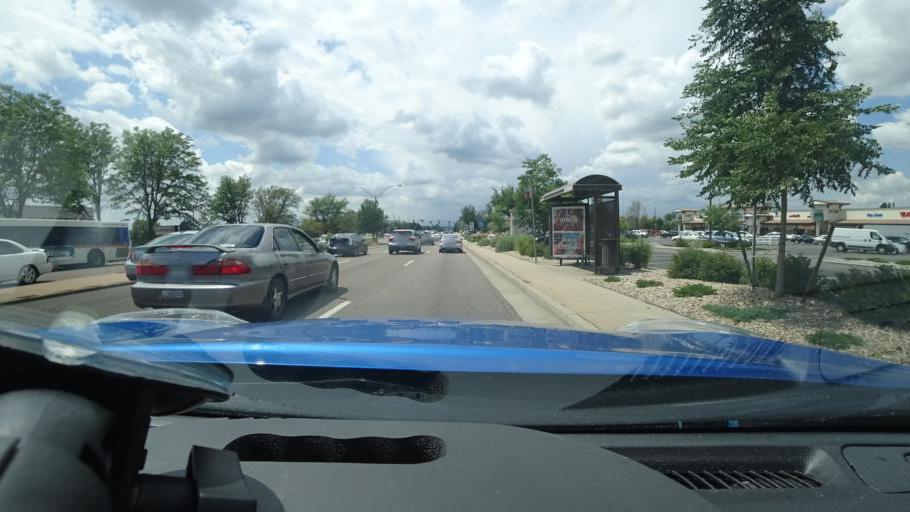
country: US
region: Colorado
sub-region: Adams County
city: Aurora
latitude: 39.6967
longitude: -104.8451
